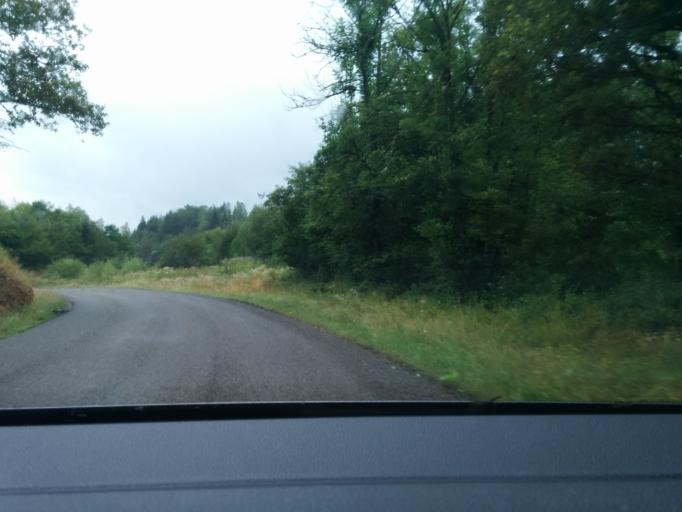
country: FR
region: Franche-Comte
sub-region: Departement du Jura
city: Saint-Lupicin
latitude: 46.4287
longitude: 5.8089
